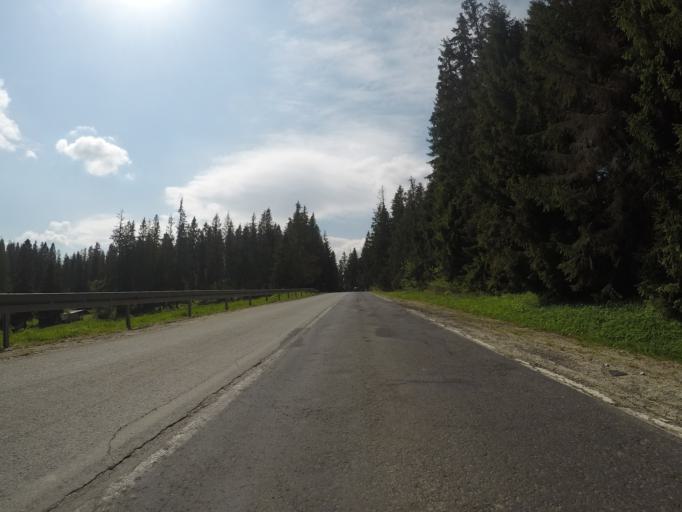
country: PL
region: Lesser Poland Voivodeship
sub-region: Powiat tatrzanski
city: Bukowina Tatrzanska
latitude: 49.3077
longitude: 20.1118
